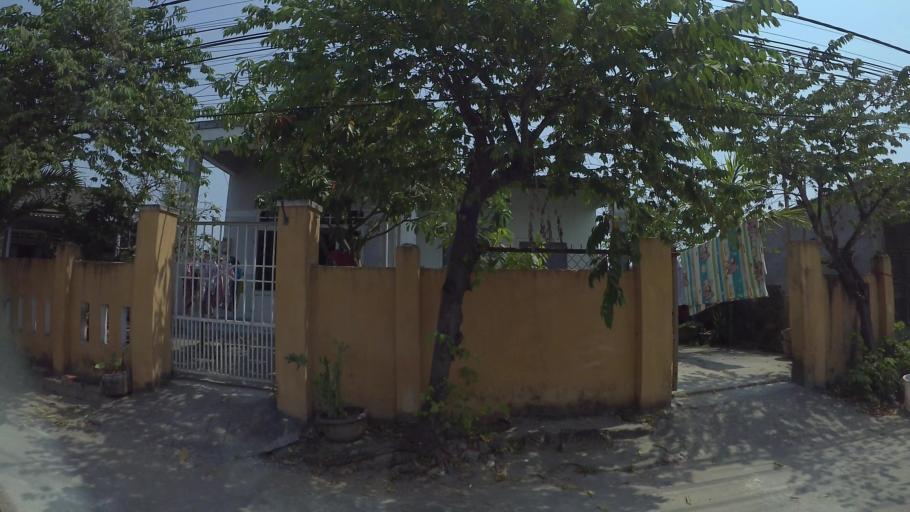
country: VN
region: Da Nang
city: Ngu Hanh Son
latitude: 16.0084
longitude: 108.2530
